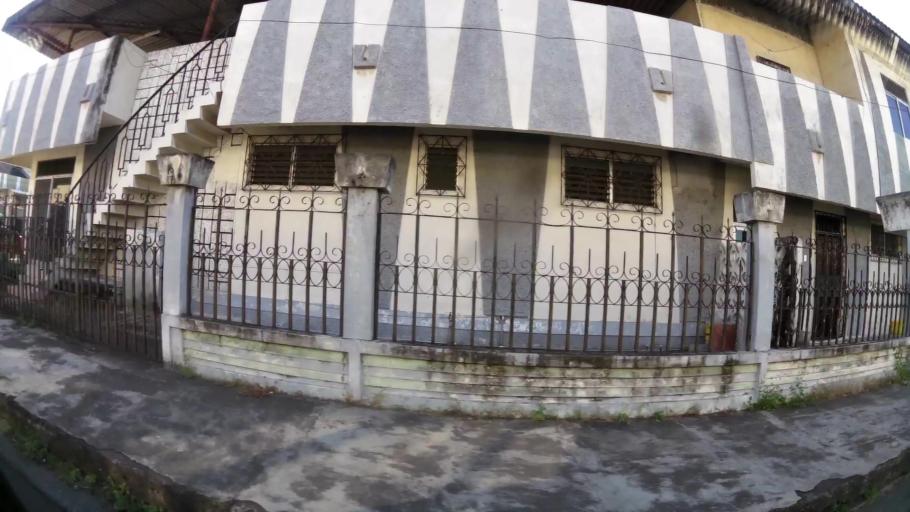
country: EC
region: Guayas
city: Eloy Alfaro
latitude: -2.1678
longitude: -79.8843
